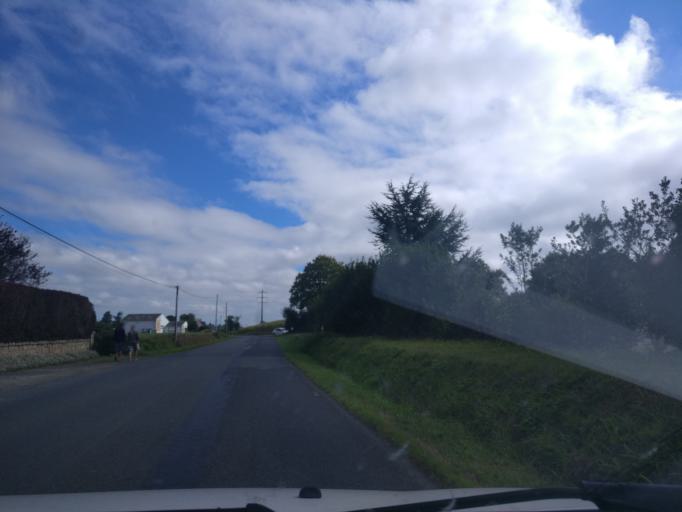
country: FR
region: Brittany
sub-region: Departement des Cotes-d'Armor
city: Rospez
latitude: 48.7246
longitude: -3.3929
